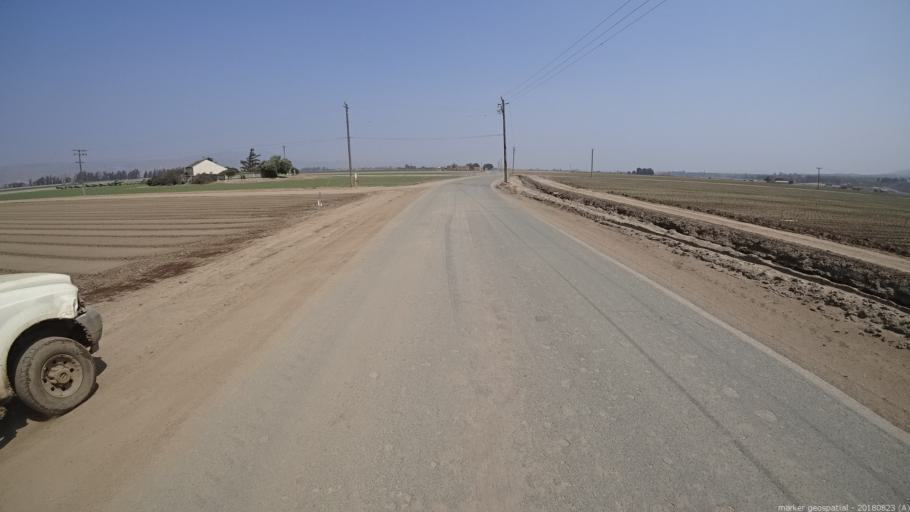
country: US
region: California
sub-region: Monterey County
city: Soledad
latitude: 36.4086
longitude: -121.3740
